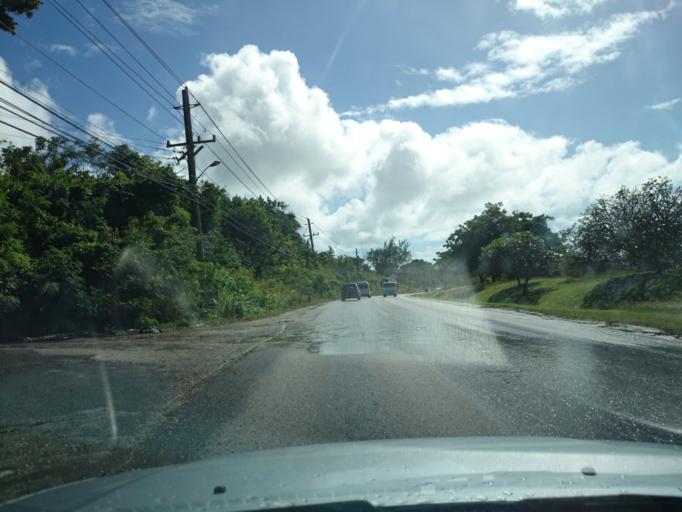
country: BB
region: Saint James
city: Holetown
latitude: 13.1690
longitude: -59.6128
